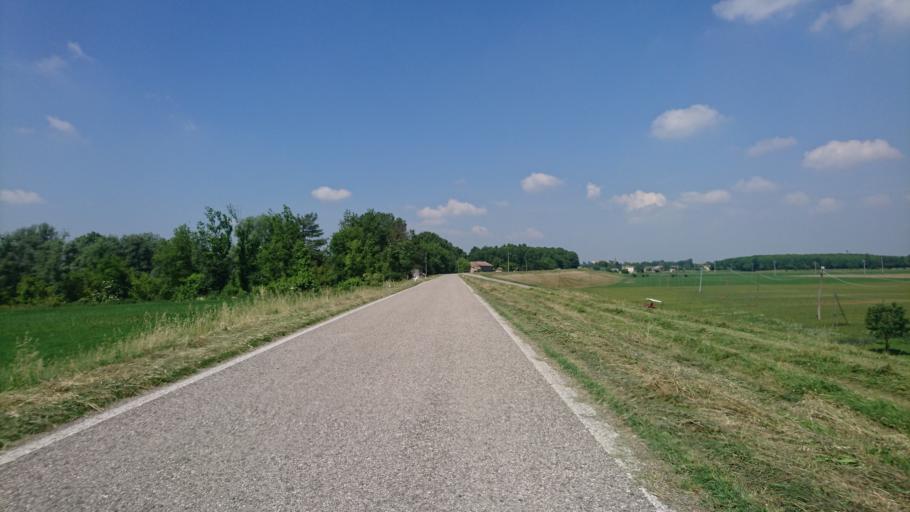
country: IT
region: Lombardy
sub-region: Provincia di Mantova
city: Sustinente
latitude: 45.0764
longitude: 10.9760
